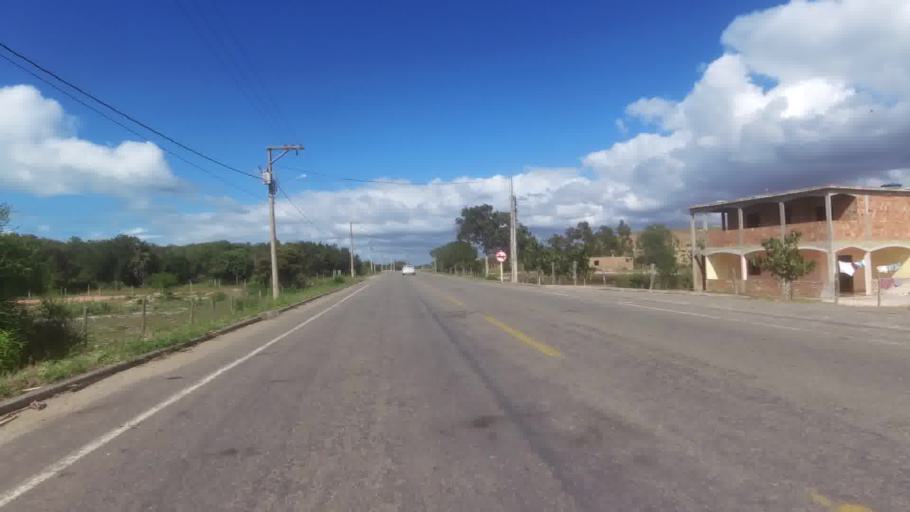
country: BR
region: Espirito Santo
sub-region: Marataizes
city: Marataizes
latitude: -21.1971
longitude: -40.9444
